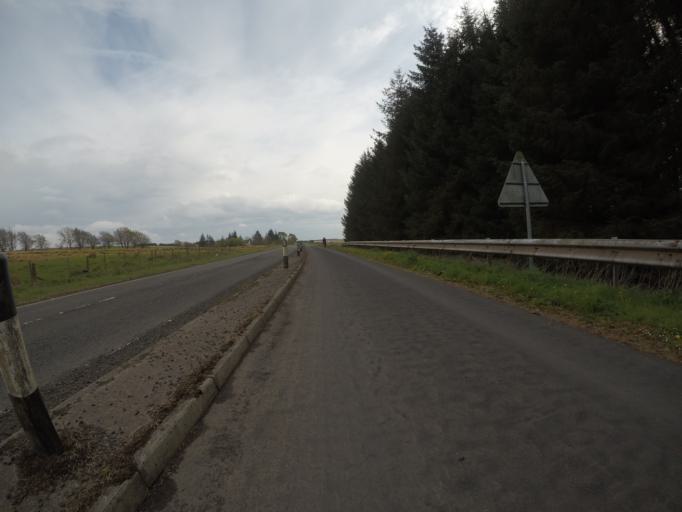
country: GB
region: Scotland
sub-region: East Renfrewshire
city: Neilston
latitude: 55.7128
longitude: -4.3996
